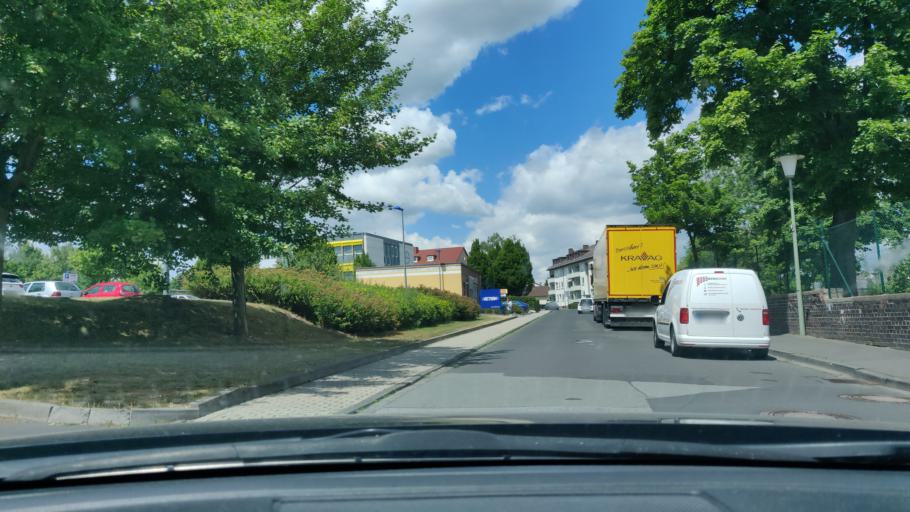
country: DE
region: Hesse
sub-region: Regierungsbezirk Kassel
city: Fuldabruck
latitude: 51.2906
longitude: 9.4569
